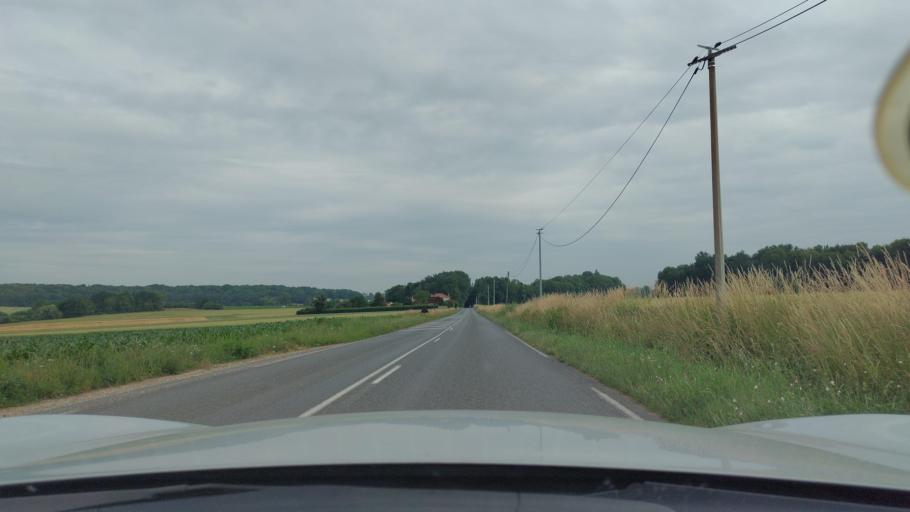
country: FR
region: Ile-de-France
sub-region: Departement de Seine-et-Marne
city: Cregy-les-Meaux
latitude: 48.9918
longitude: 2.8775
